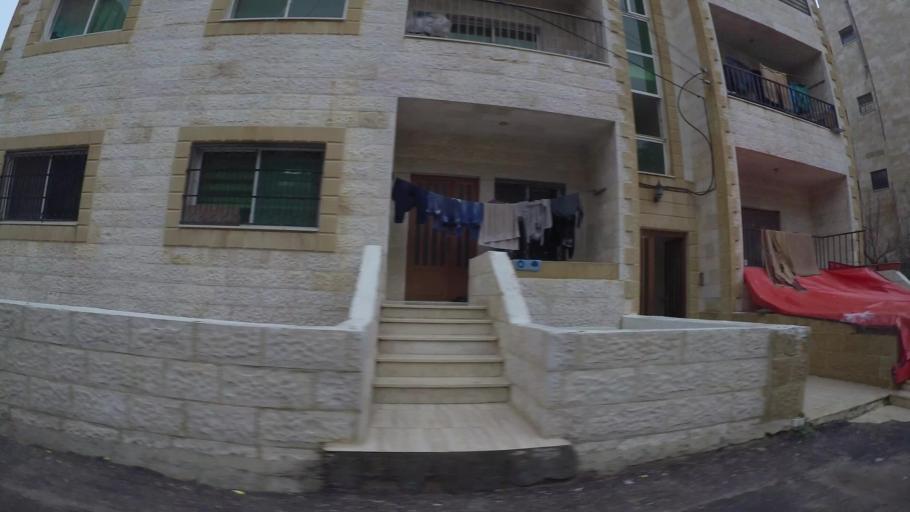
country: JO
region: Amman
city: Al Jubayhah
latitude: 32.0276
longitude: 35.8372
